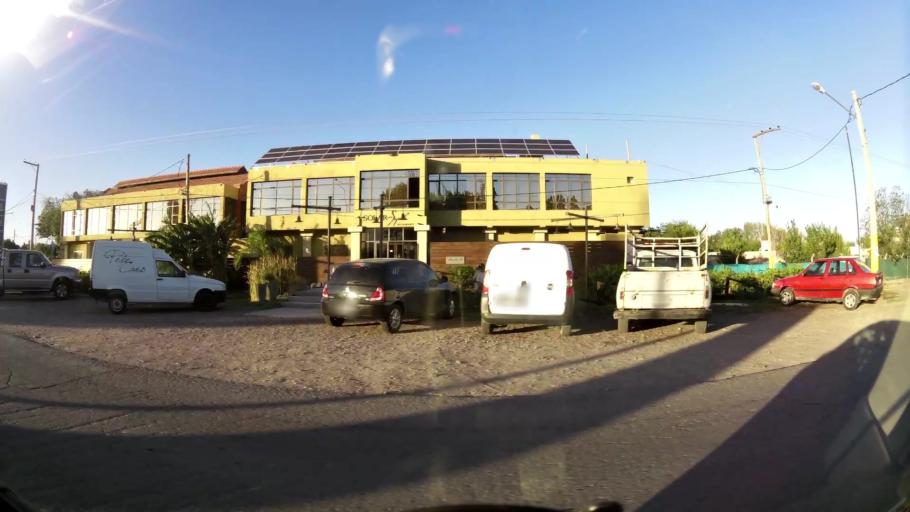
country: AR
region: San Juan
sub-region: Departamento de Santa Lucia
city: Santa Lucia
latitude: -31.5466
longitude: -68.4878
